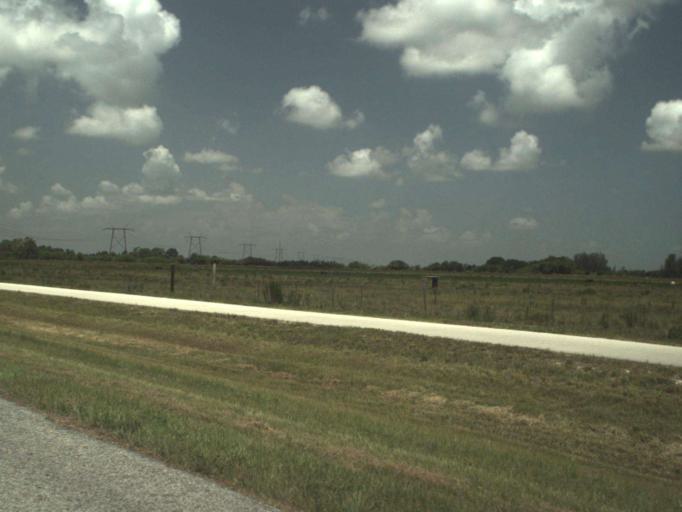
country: US
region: Florida
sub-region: Saint Lucie County
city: Fort Pierce South
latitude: 27.3846
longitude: -80.4679
